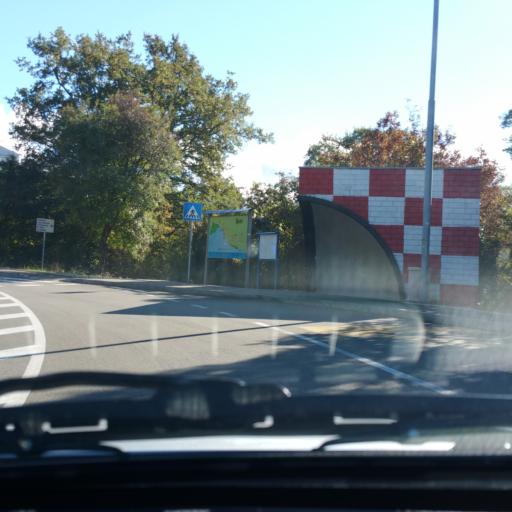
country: HR
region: Primorsko-Goranska
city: Njivice
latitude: 45.1547
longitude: 14.5369
